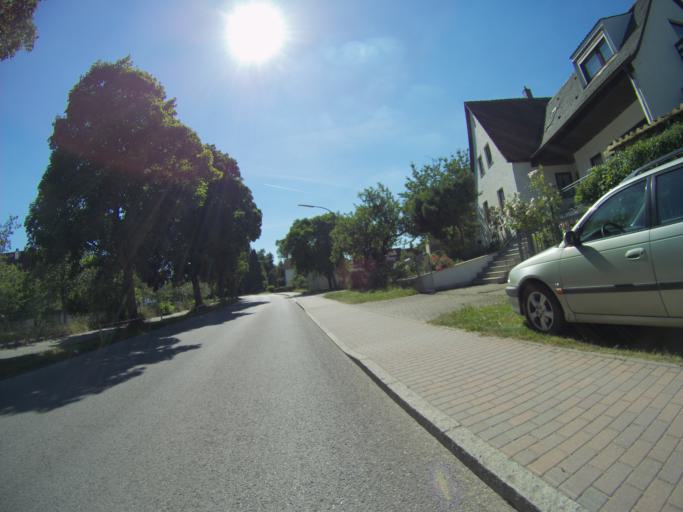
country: DE
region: Bavaria
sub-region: Upper Bavaria
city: Freising
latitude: 48.3949
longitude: 11.7098
